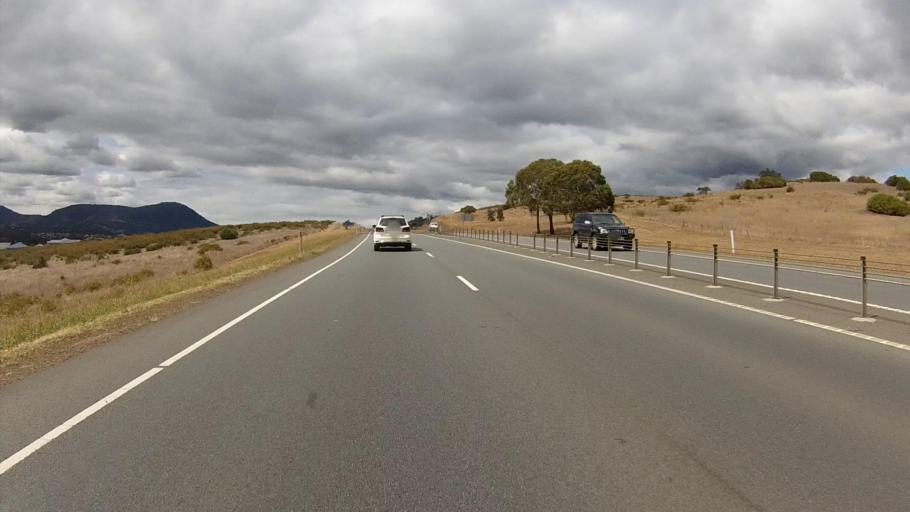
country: AU
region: Tasmania
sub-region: Glenorchy
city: Granton
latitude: -42.7583
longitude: 147.2312
